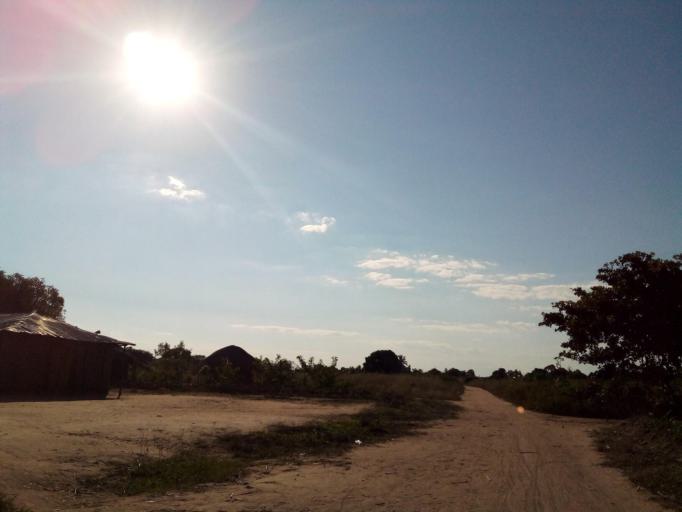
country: MZ
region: Zambezia
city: Quelimane
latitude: -17.5126
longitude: 36.6846
